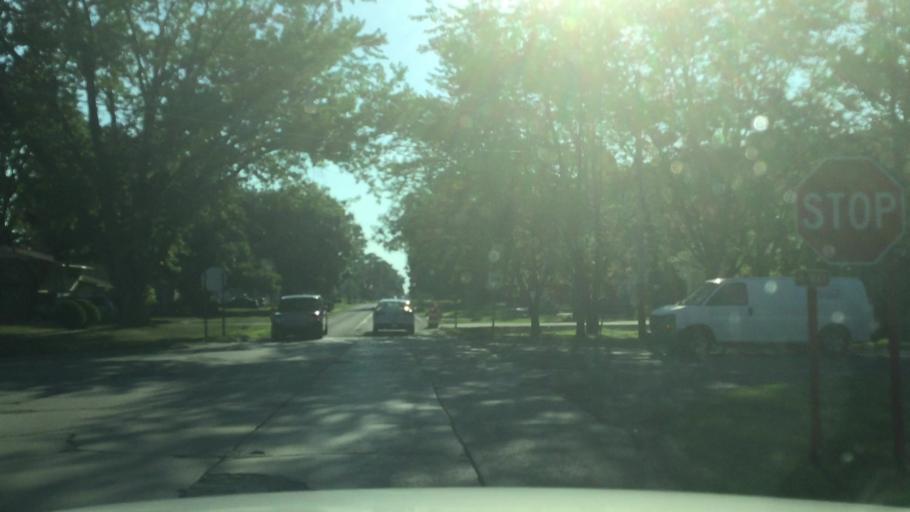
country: US
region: Michigan
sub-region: Wayne County
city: Westland
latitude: 42.3174
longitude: -83.3789
